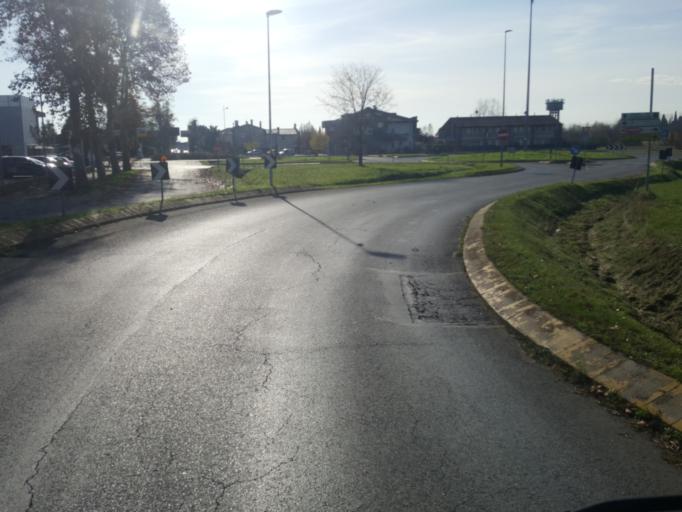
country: IT
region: Veneto
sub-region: Provincia di Treviso
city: Riese Pio X
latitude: 45.7347
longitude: 11.9119
